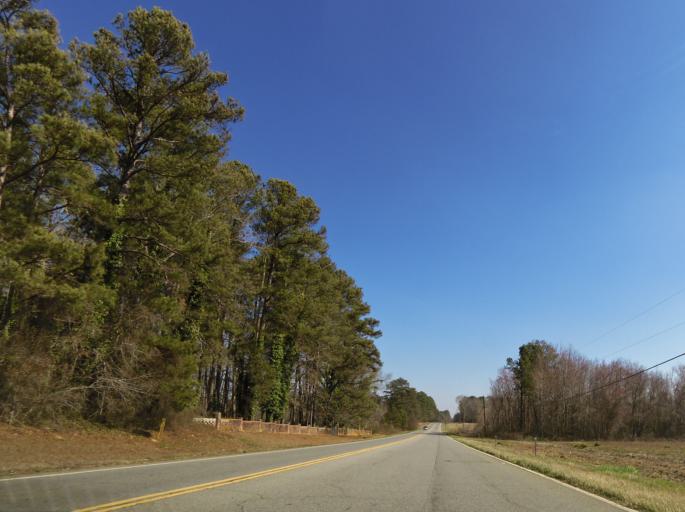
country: US
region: Georgia
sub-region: Bleckley County
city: Cochran
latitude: 32.3638
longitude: -83.3824
